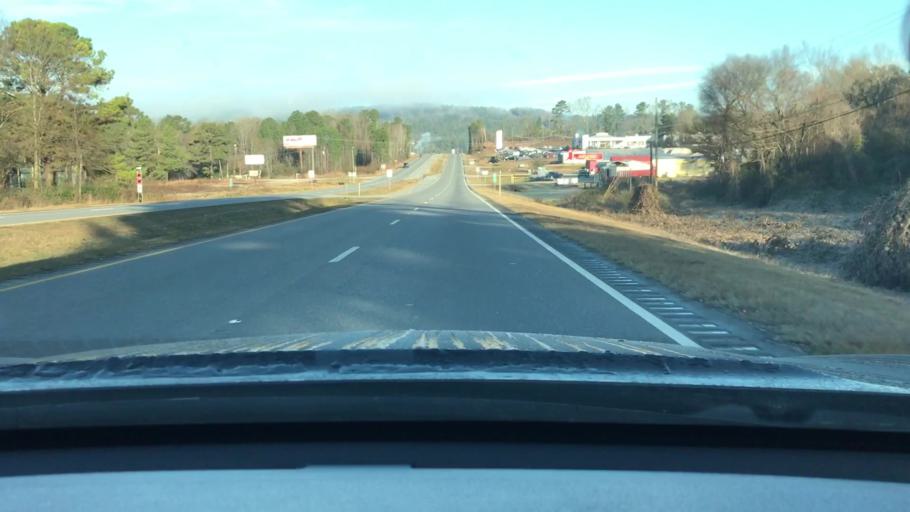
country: US
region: Alabama
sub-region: Talladega County
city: Mignon
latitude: 33.1848
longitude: -86.3020
